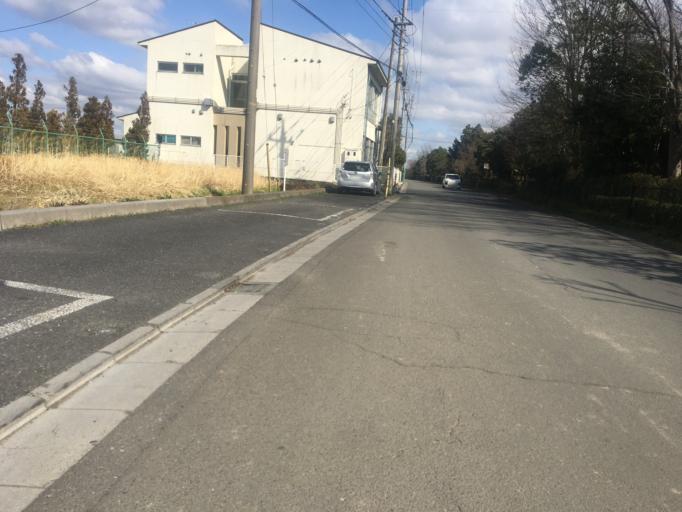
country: JP
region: Saitama
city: Shiki
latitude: 35.8777
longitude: 139.5879
